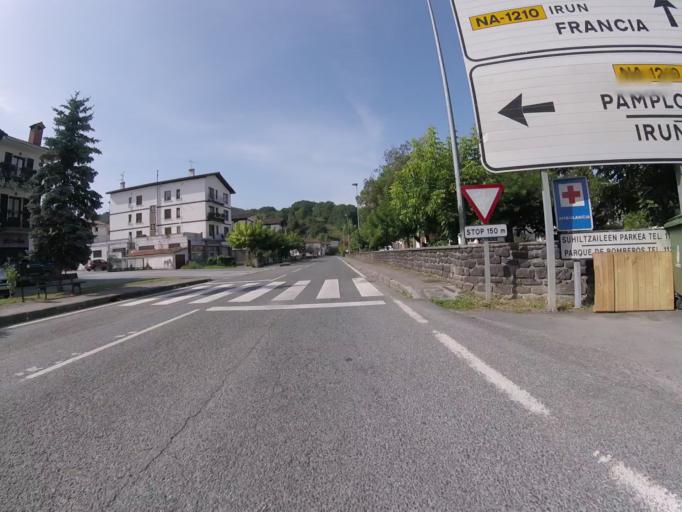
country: ES
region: Navarre
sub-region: Provincia de Navarra
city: Doneztebe
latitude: 43.1385
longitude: -1.6090
